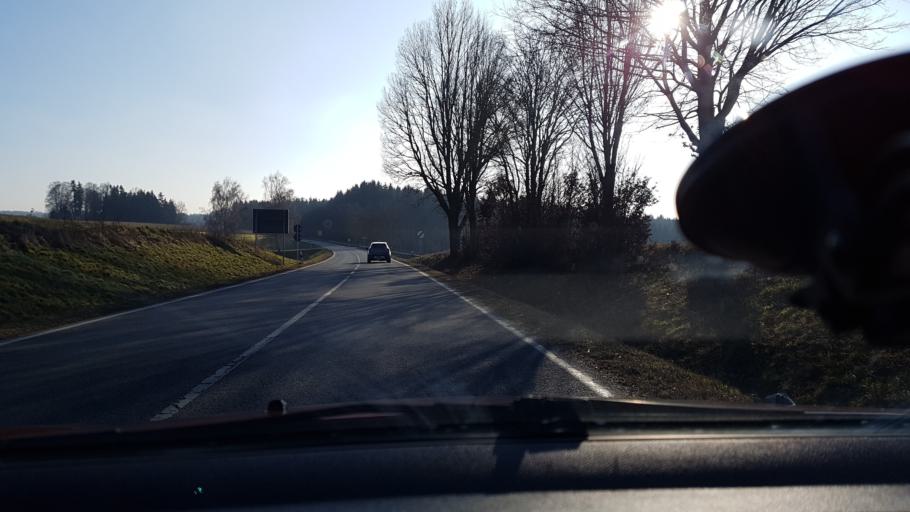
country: DE
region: Bavaria
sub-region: Lower Bavaria
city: Reut
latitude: 48.3178
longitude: 12.9524
